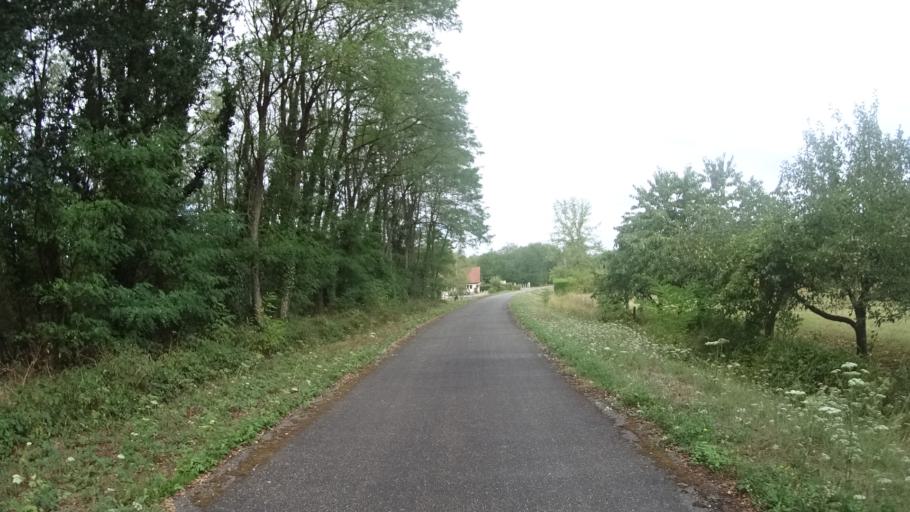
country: FR
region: Auvergne
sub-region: Departement de l'Allier
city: Diou
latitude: 46.5395
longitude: 3.7519
